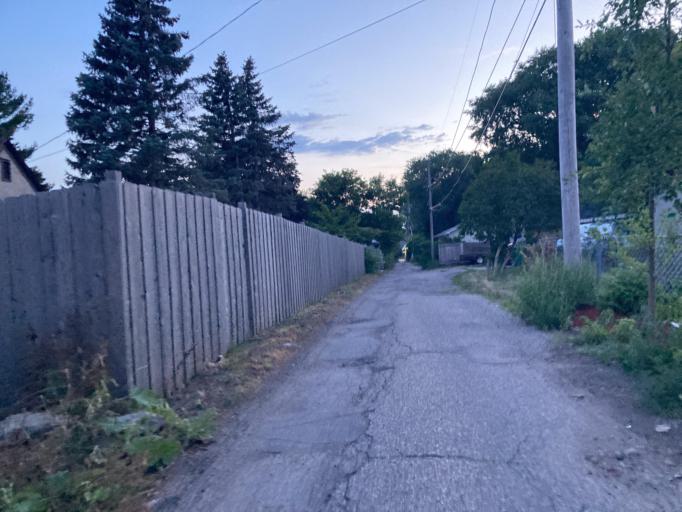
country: US
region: Minnesota
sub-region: Dakota County
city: West Saint Paul
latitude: 44.9183
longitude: -93.0775
